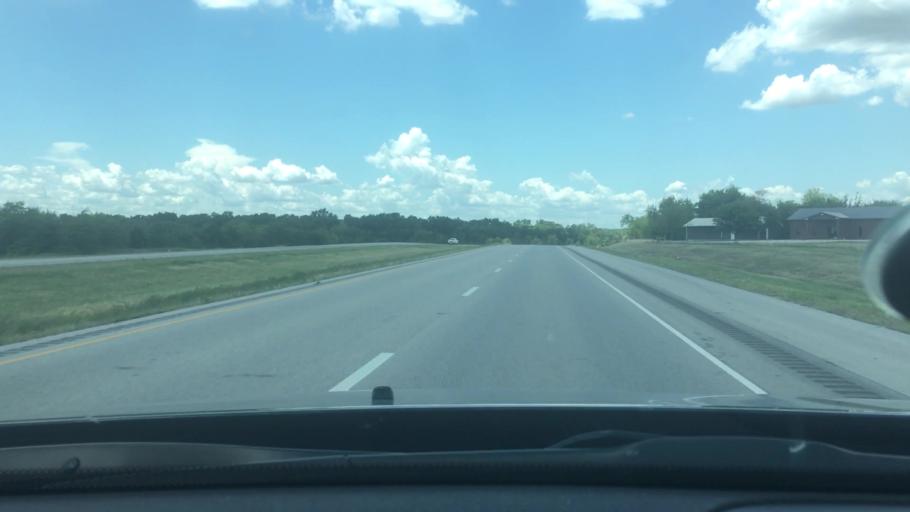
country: US
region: Oklahoma
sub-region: Bryan County
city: Calera
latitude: 33.9778
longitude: -96.4255
